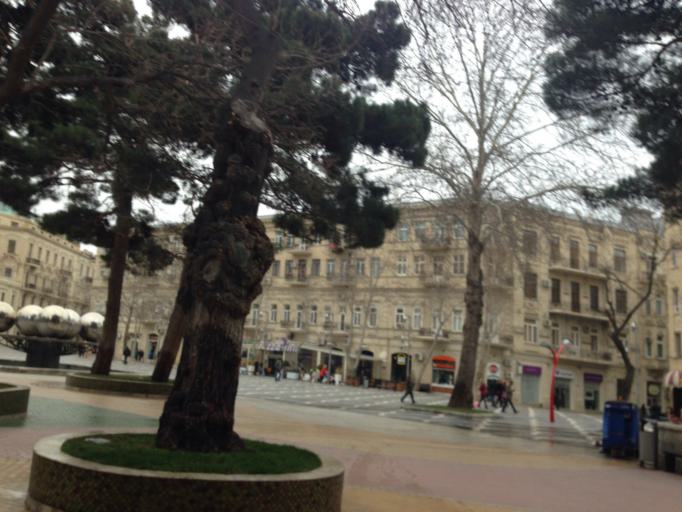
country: AZ
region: Baki
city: Badamdar
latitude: 40.3712
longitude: 49.8373
